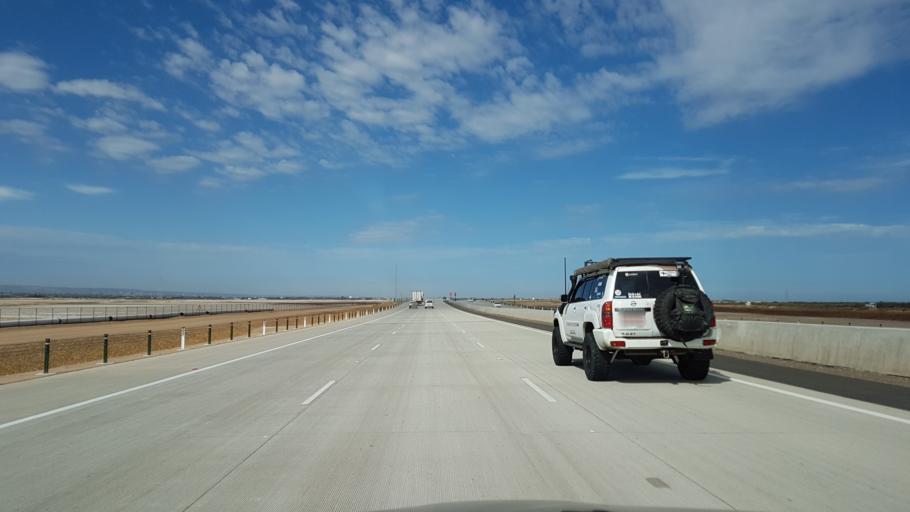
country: AU
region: South Australia
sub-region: Port Adelaide Enfield
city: Enfield
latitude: -34.7974
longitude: 138.5775
